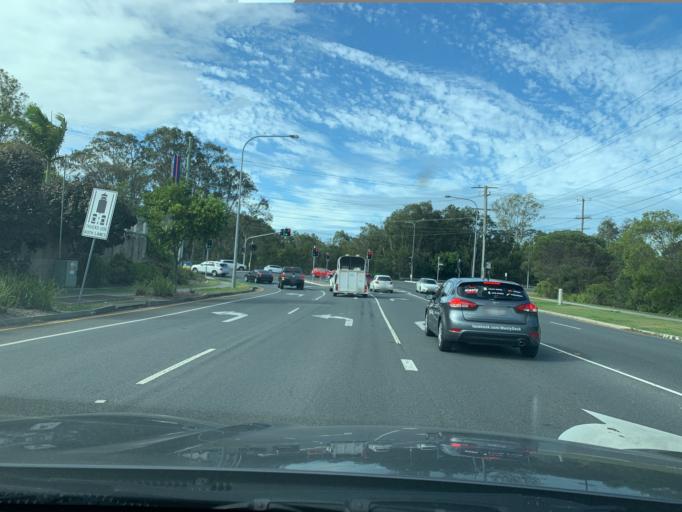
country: AU
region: Queensland
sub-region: Brisbane
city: Wynnum West
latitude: -27.4768
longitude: 153.1406
